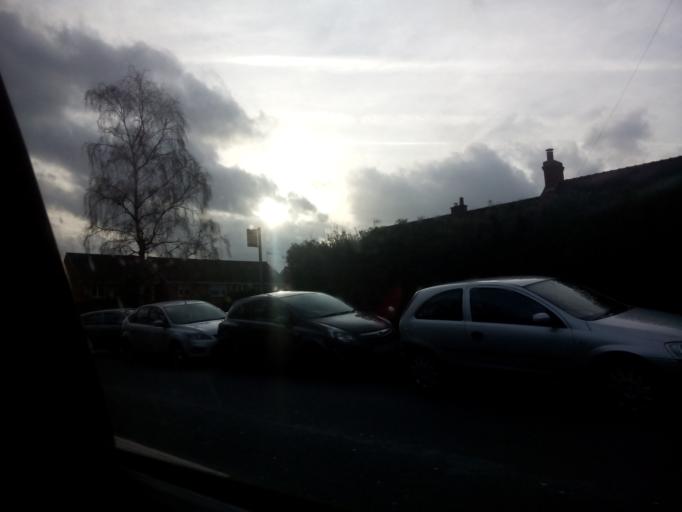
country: GB
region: England
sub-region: Worcestershire
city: Bromsgrove
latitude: 52.3629
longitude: -2.0467
